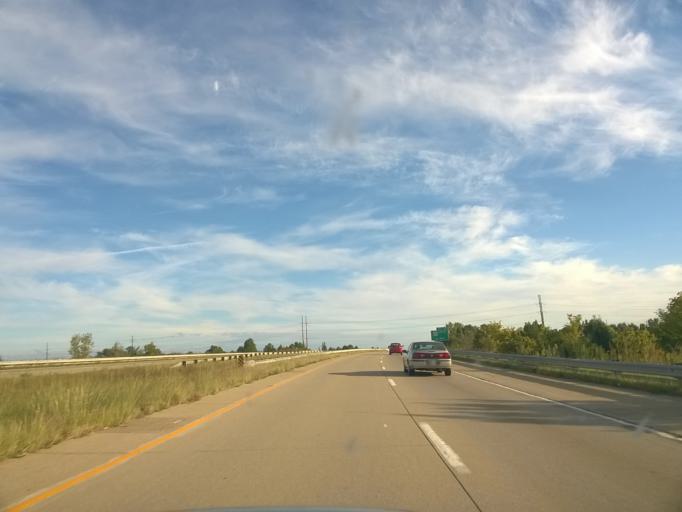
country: US
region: Indiana
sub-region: Vanderburgh County
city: Melody Hill
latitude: 38.1190
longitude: -87.4790
